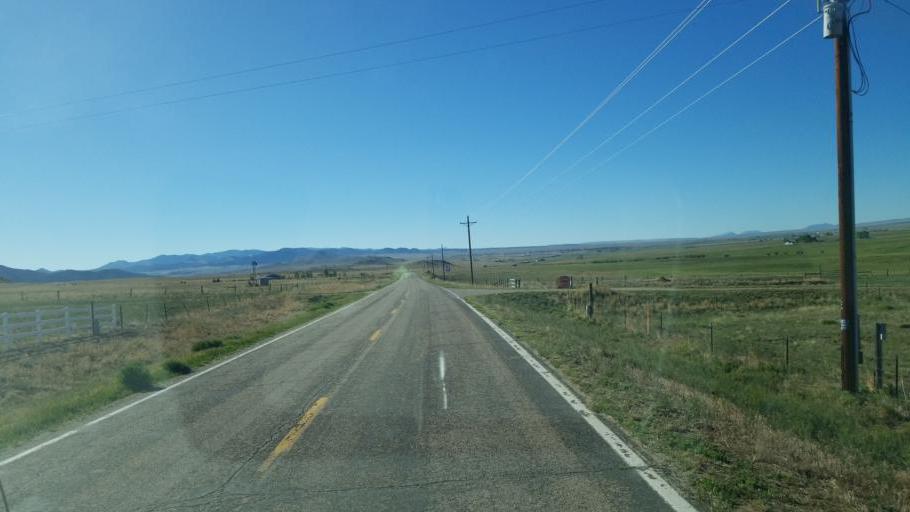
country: US
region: Colorado
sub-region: Custer County
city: Westcliffe
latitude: 38.1924
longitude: -105.5229
